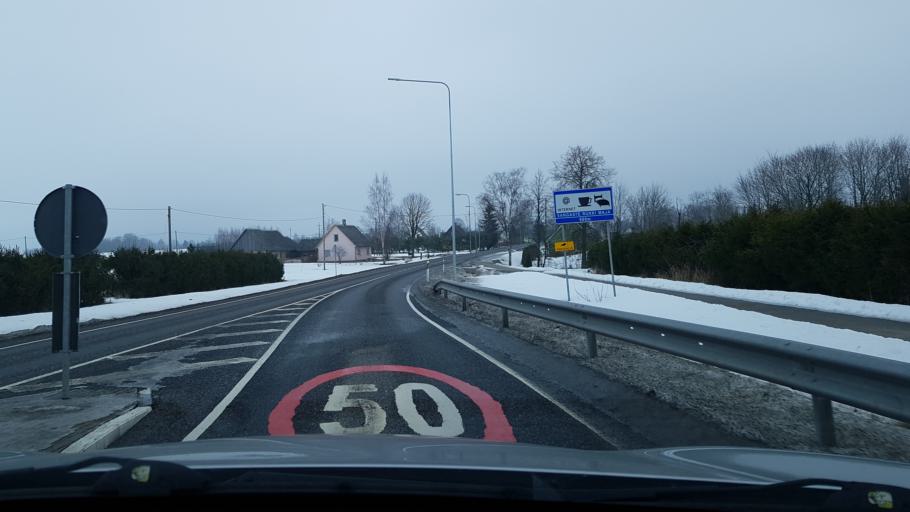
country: EE
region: Vorumaa
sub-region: Antsla vald
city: Vana-Antsla
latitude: 57.9225
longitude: 26.3187
